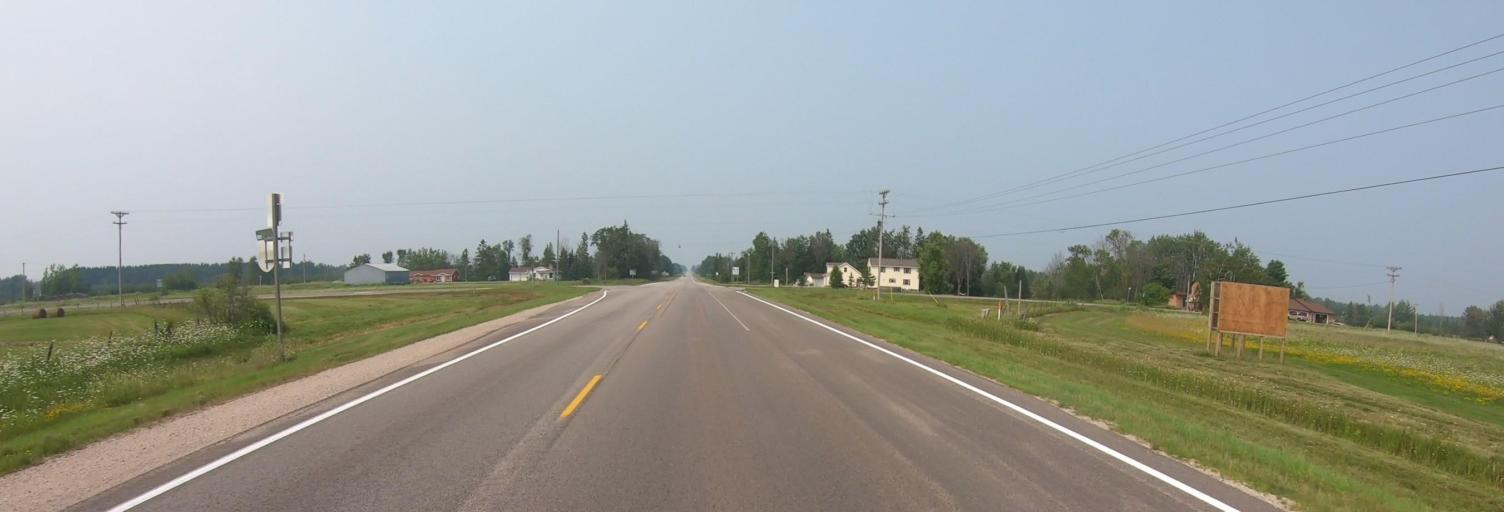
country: US
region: Michigan
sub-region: Chippewa County
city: Sault Ste. Marie
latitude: 46.1862
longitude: -84.3635
